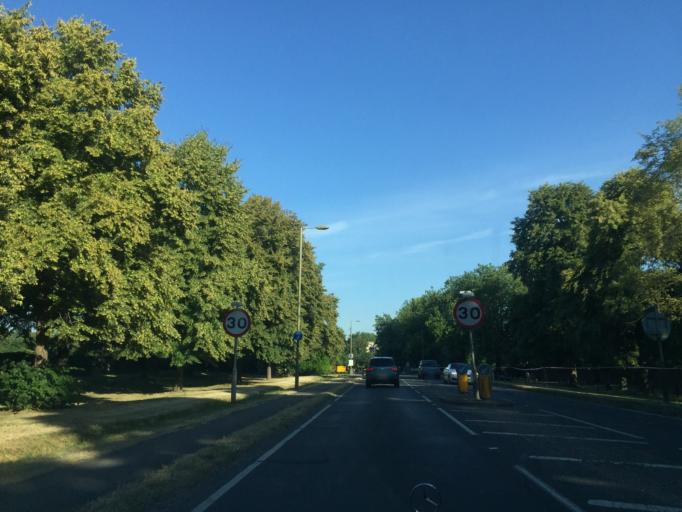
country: GB
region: England
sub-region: Oxfordshire
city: Henley on Thames
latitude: 51.5459
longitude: -0.9136
